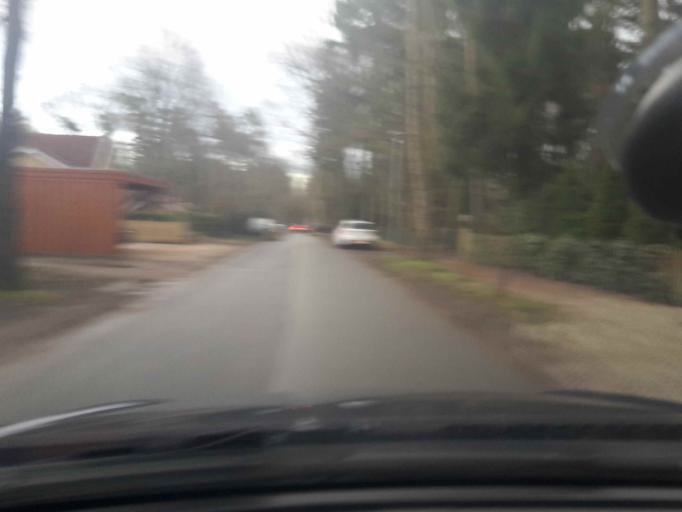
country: DE
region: Lower Saxony
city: Buchholz in der Nordheide
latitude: 53.2856
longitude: 9.8791
